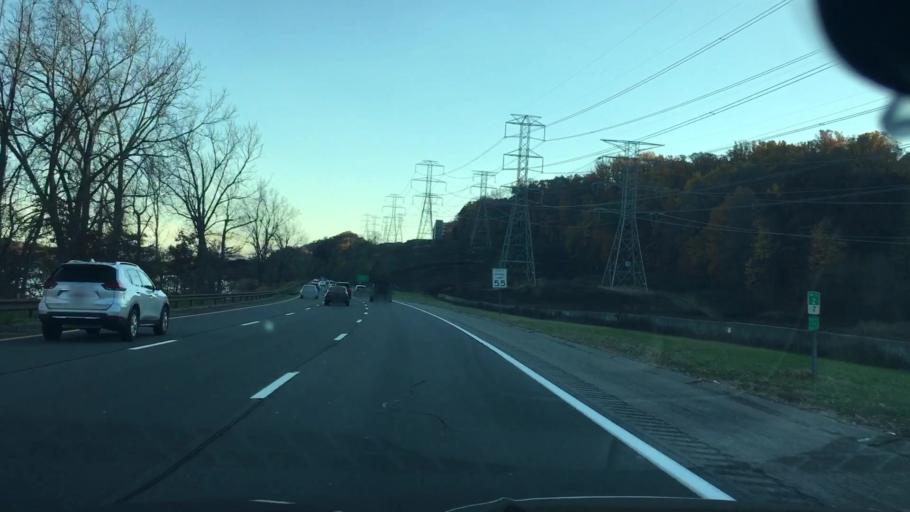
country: US
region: New York
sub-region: Westchester County
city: Tuckahoe
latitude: 40.9716
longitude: -73.8531
